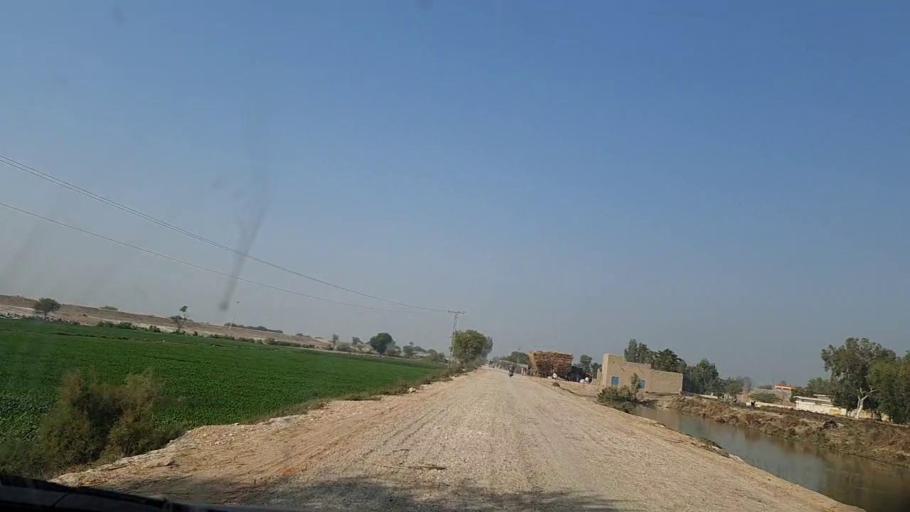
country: PK
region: Sindh
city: Moro
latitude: 26.7381
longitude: 67.9190
